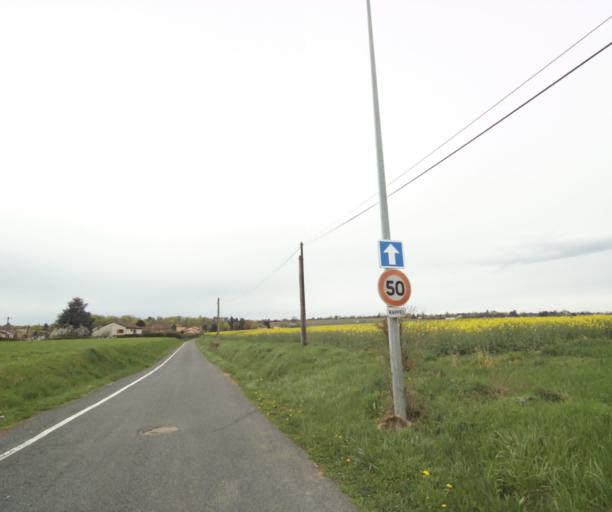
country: FR
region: Bourgogne
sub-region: Departement de Saone-et-Loire
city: Charnay-les-Macon
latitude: 46.3123
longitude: 4.8031
